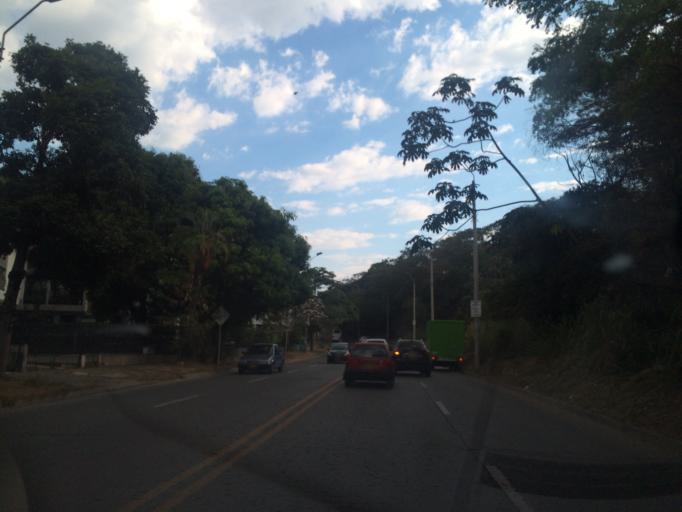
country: CO
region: Valle del Cauca
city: Cali
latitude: 3.4048
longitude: -76.5559
